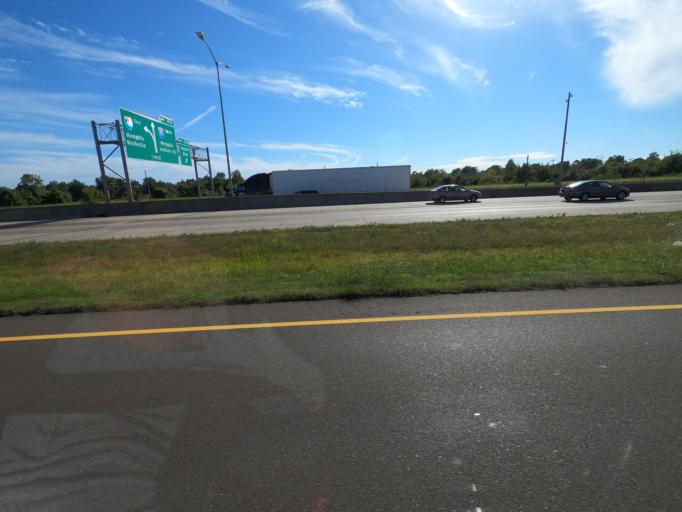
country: US
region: Arkansas
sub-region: Crittenden County
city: West Memphis
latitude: 35.1614
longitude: -90.1655
